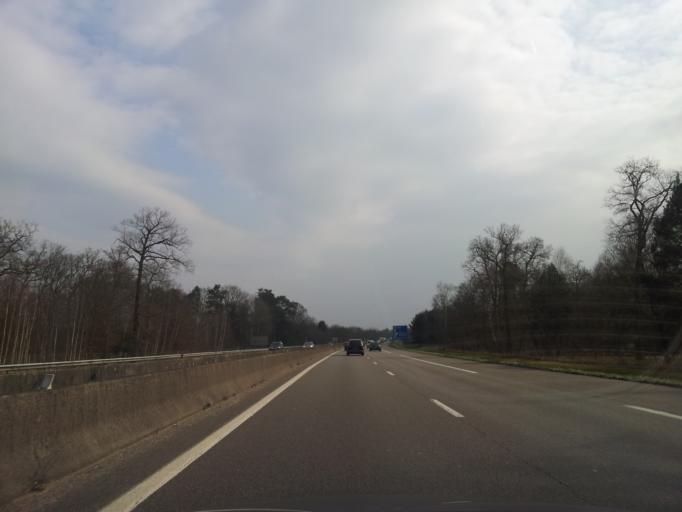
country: FR
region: Alsace
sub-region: Departement du Bas-Rhin
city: Eckwersheim
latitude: 48.6963
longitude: 7.7223
